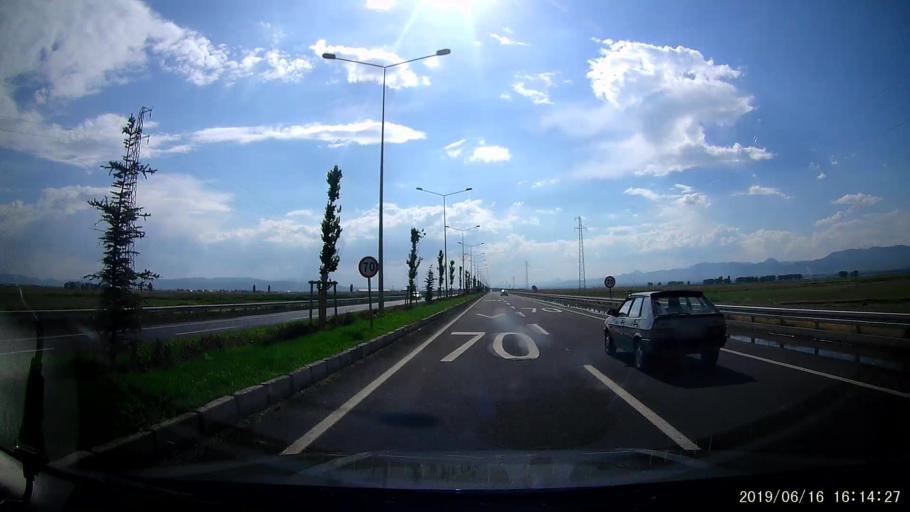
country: TR
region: Erzurum
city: Erzurum
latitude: 39.9607
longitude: 41.2487
